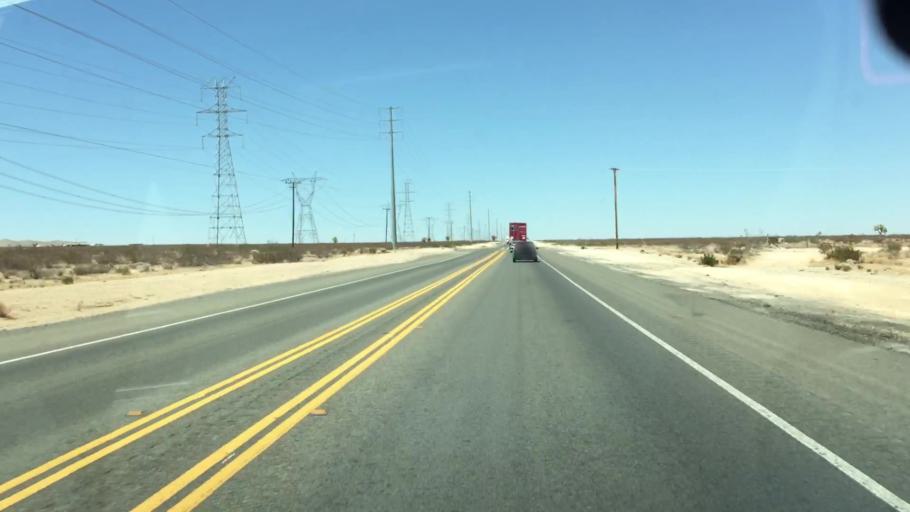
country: US
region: California
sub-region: San Bernardino County
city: Adelanto
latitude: 34.7031
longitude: -117.4543
